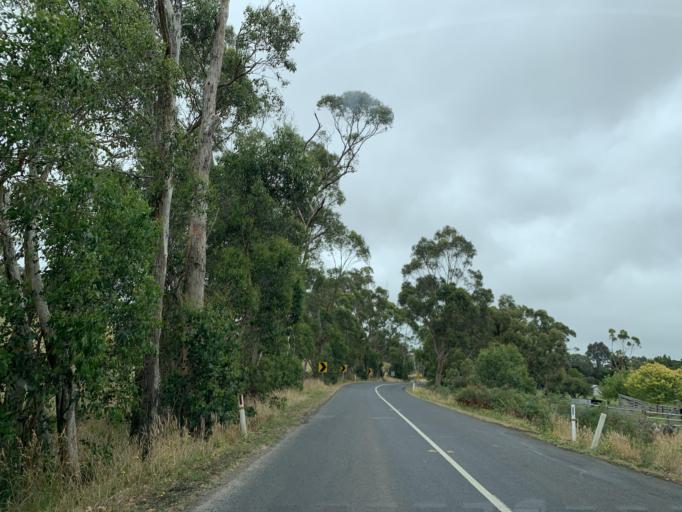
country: AU
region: Victoria
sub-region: Cardinia
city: Bunyip
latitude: -38.3303
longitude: 145.7056
